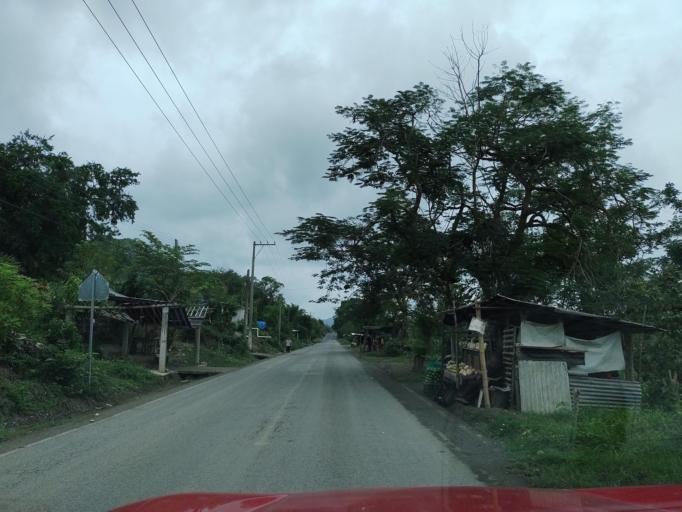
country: MX
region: Puebla
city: Espinal
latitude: 20.2632
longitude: -97.3527
